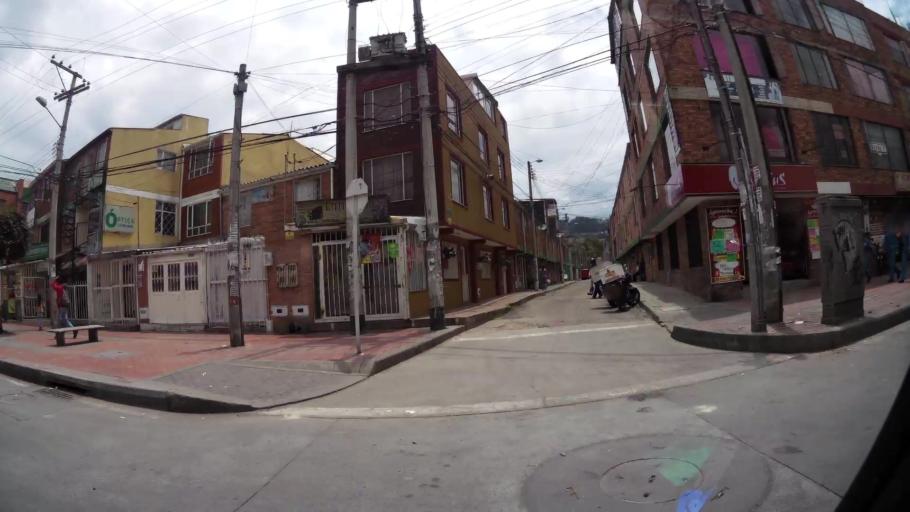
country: CO
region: Cundinamarca
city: Cota
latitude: 4.7631
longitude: -74.0374
